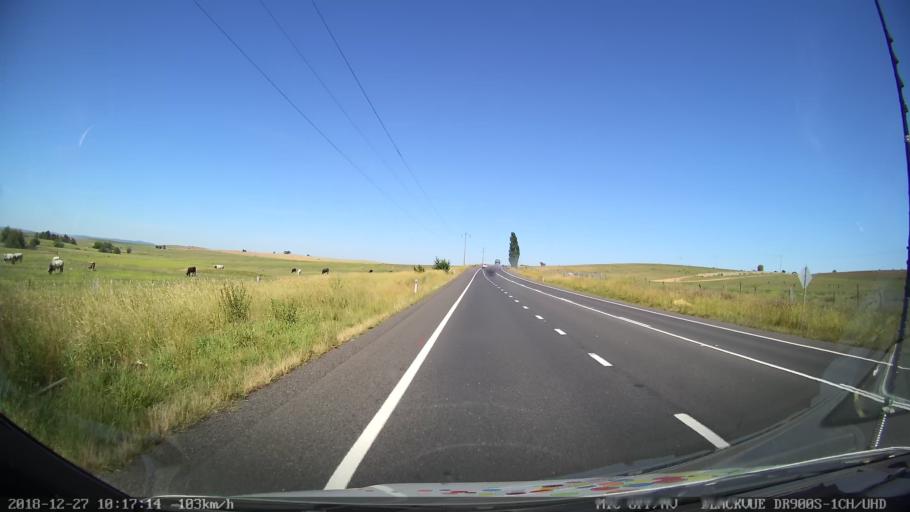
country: AU
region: New South Wales
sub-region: Bathurst Regional
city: Kelso
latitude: -33.4262
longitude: 149.6816
